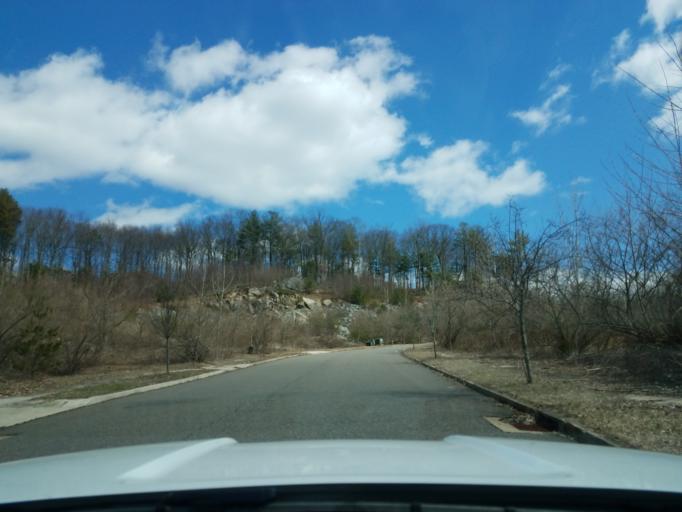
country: US
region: Connecticut
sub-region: New Haven County
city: Naugatuck
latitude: 41.4730
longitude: -73.0305
